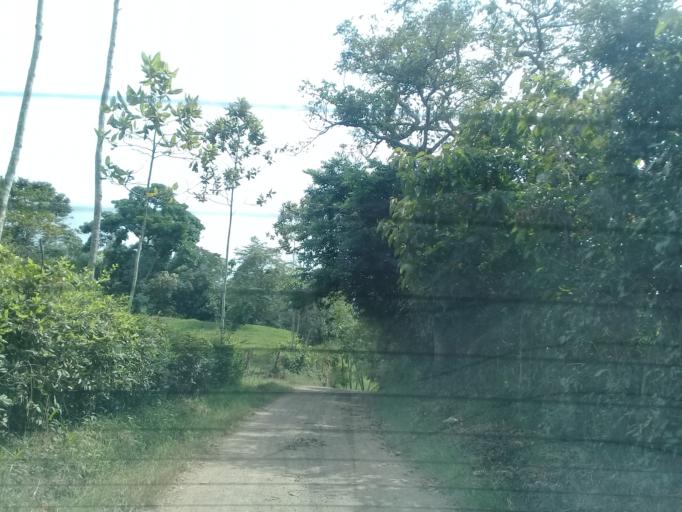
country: CO
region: Cundinamarca
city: Guaduas
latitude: 5.0423
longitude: -74.6091
